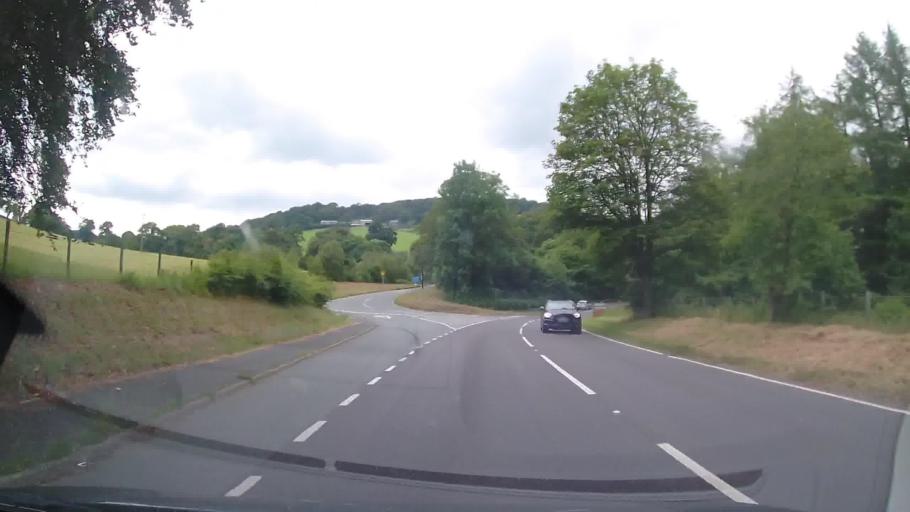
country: GB
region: Wales
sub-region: Gwynedd
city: Bala
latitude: 52.9167
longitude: -3.6061
